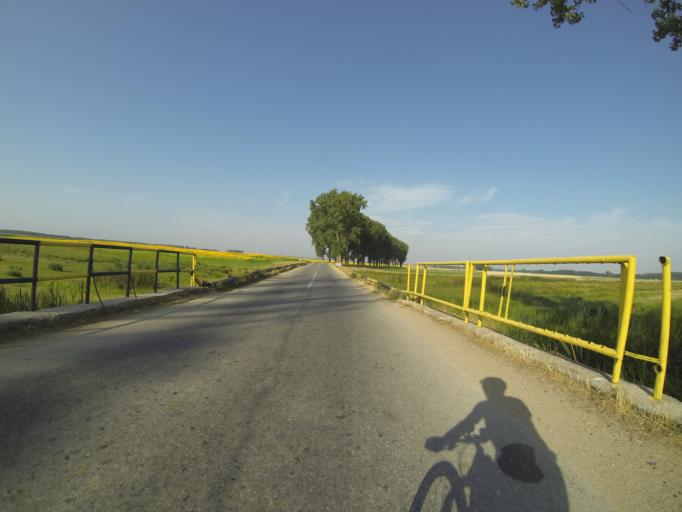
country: RO
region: Dolj
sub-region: Comuna Dobresti
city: Dobresti
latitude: 43.9831
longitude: 23.9197
